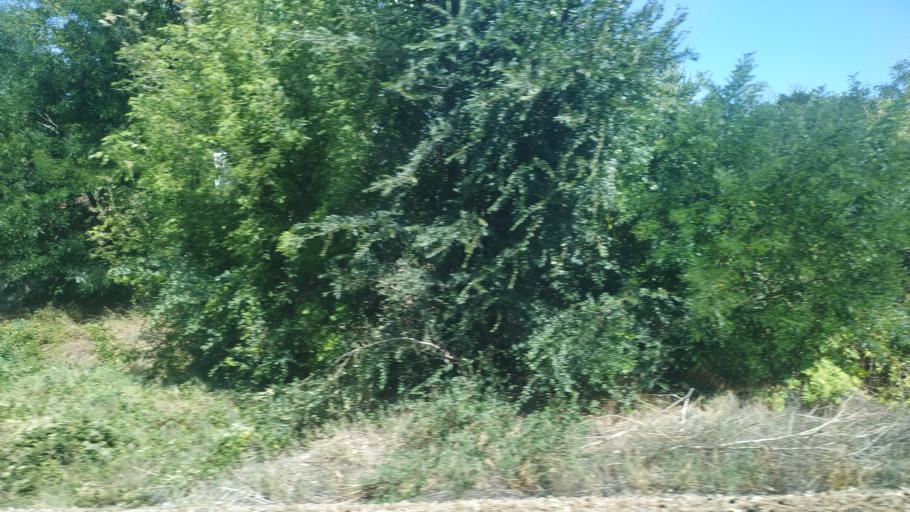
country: RO
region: Constanta
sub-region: Oras Murfatlar
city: Murfatlar
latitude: 44.1741
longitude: 28.4054
